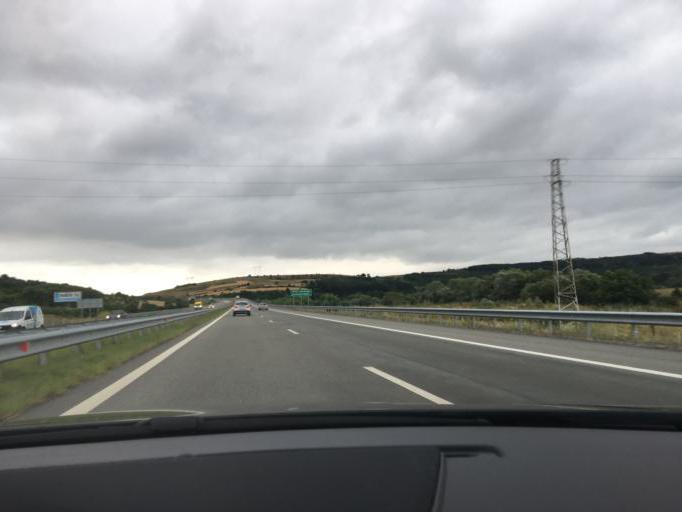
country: BG
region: Kyustendil
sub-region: Obshtina Bobovdol
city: Bobovdol
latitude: 42.3879
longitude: 23.1167
